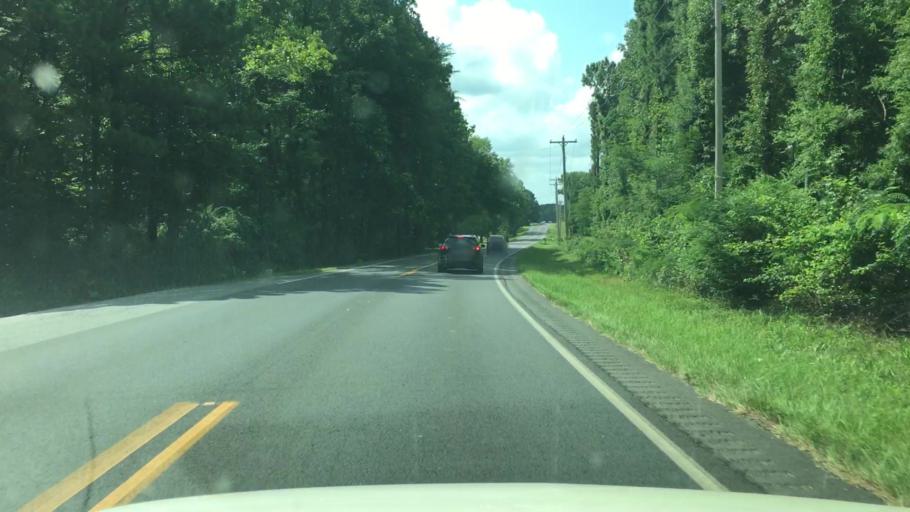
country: US
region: Arkansas
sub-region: Garland County
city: Lake Hamilton
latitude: 34.3105
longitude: -93.1684
